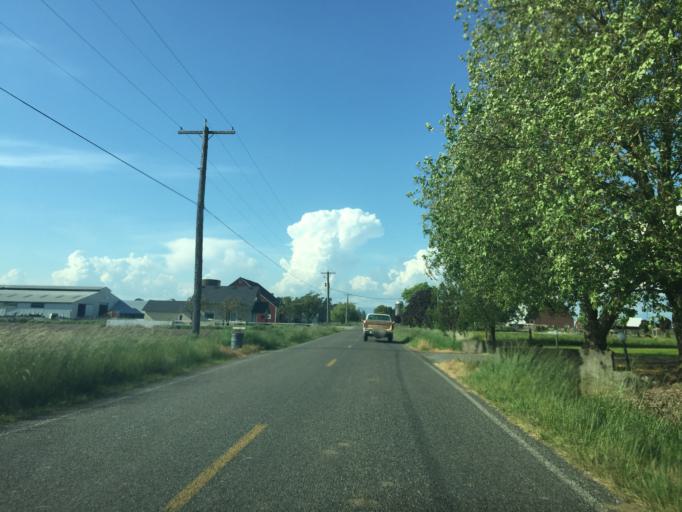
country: US
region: Washington
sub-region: Whatcom County
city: Lynden
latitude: 48.9717
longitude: -122.4408
